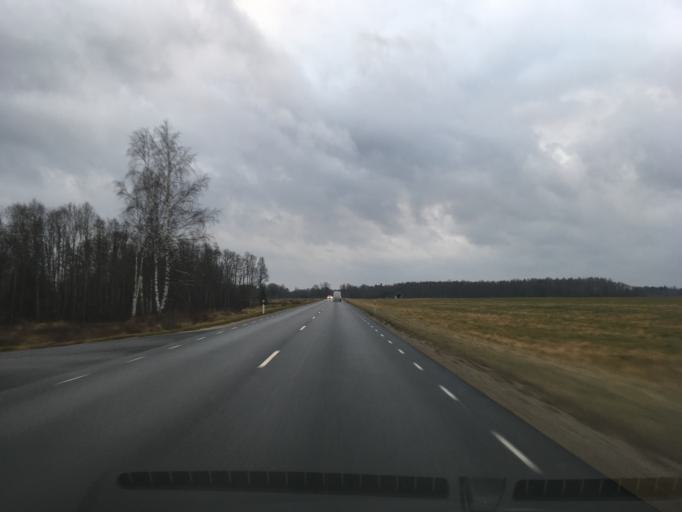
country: EE
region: Harju
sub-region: Anija vald
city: Kehra
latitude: 59.2902
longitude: 25.3755
